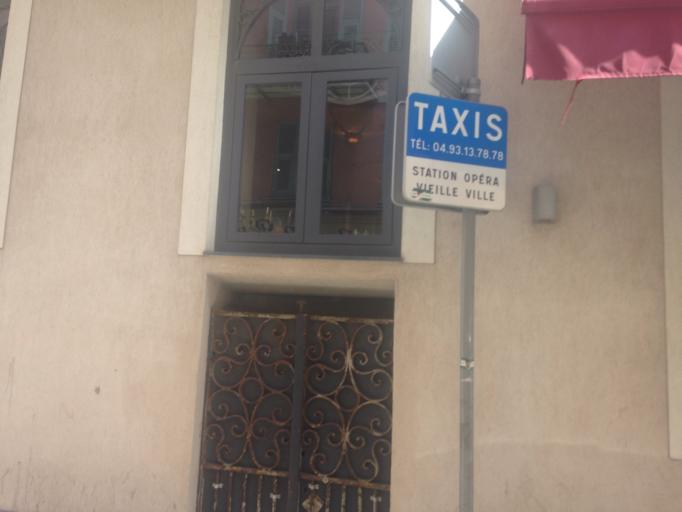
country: FR
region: Provence-Alpes-Cote d'Azur
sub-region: Departement des Alpes-Maritimes
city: Nice
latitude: 43.6960
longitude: 7.2729
